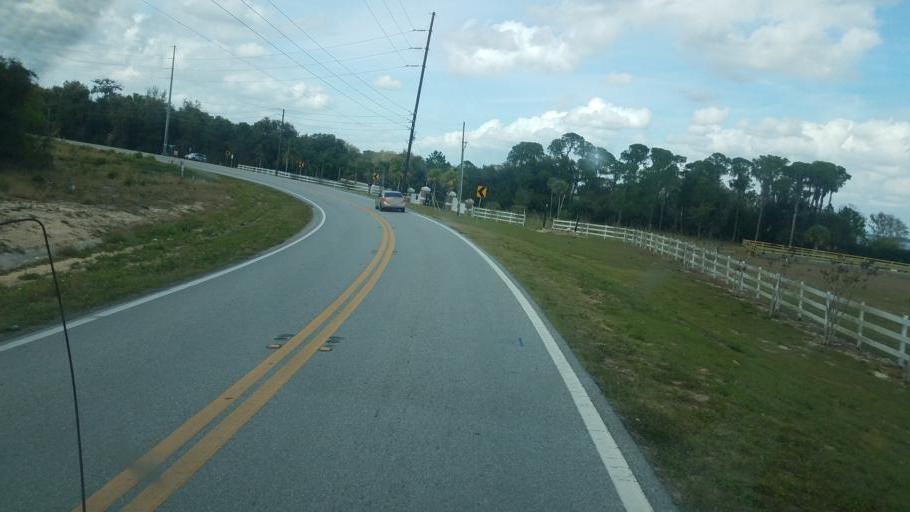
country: US
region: Florida
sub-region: Polk County
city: Lake Wales
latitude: 27.9600
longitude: -81.5379
